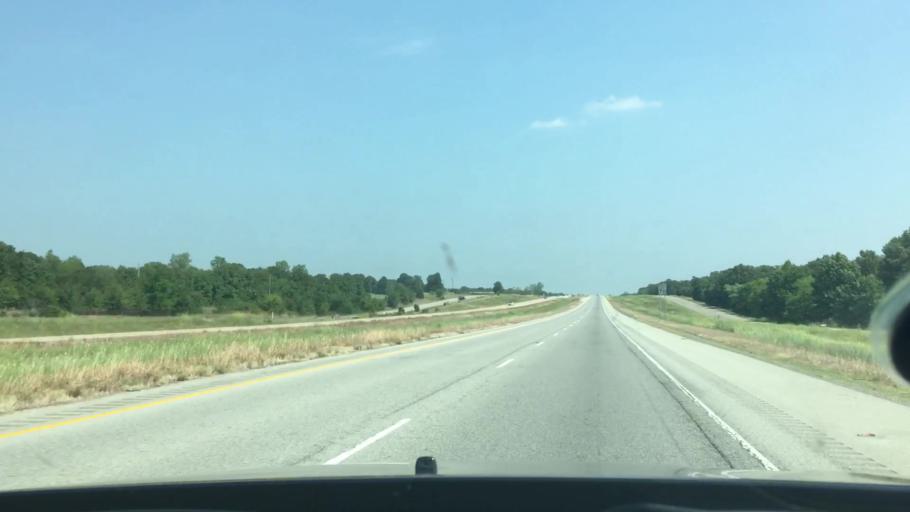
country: US
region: Oklahoma
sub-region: Atoka County
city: Atoka
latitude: 34.2753
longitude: -96.2032
